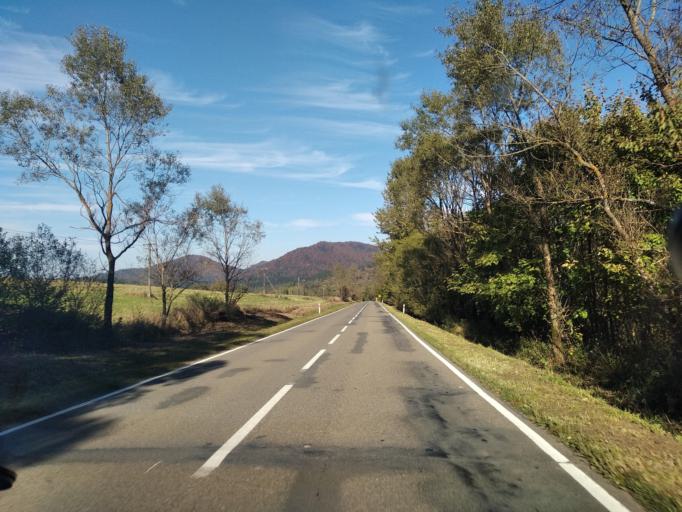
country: PL
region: Subcarpathian Voivodeship
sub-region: Powiat leski
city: Cisna
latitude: 49.2562
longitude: 22.2863
